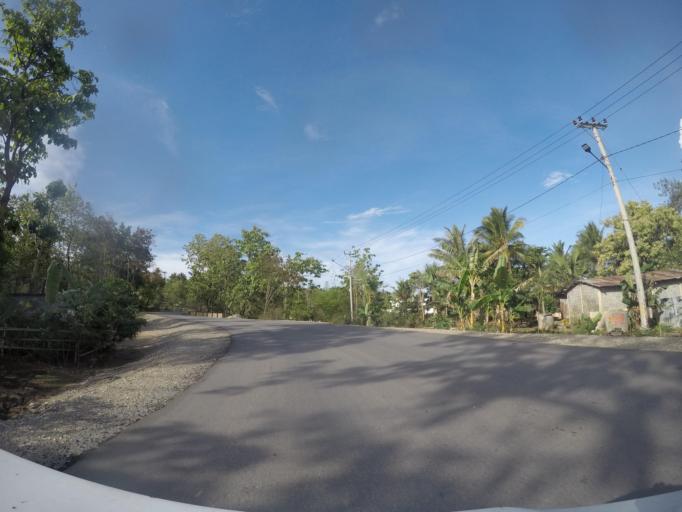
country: TL
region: Baucau
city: Baucau
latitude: -8.4948
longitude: 126.4549
